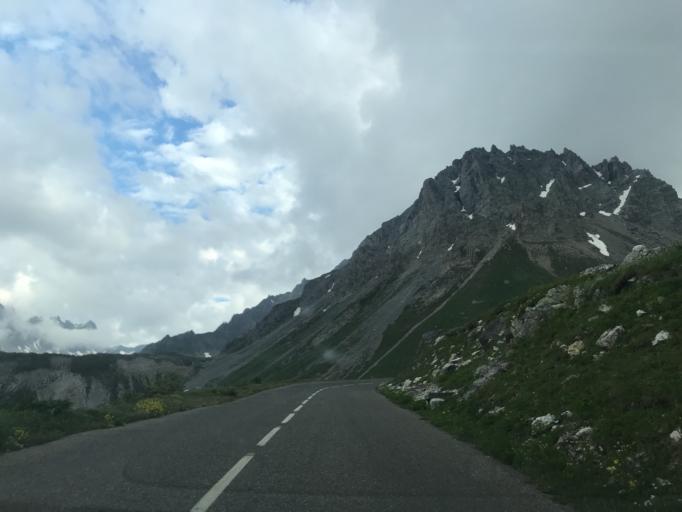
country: FR
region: Rhone-Alpes
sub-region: Departement de la Savoie
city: Valloire
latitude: 45.0865
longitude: 6.4321
